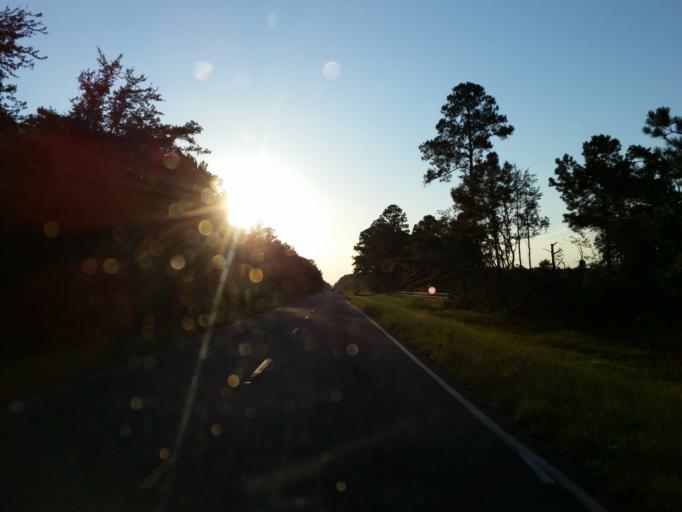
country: US
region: Georgia
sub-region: Lanier County
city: Lakeland
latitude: 31.1670
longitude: -83.0972
